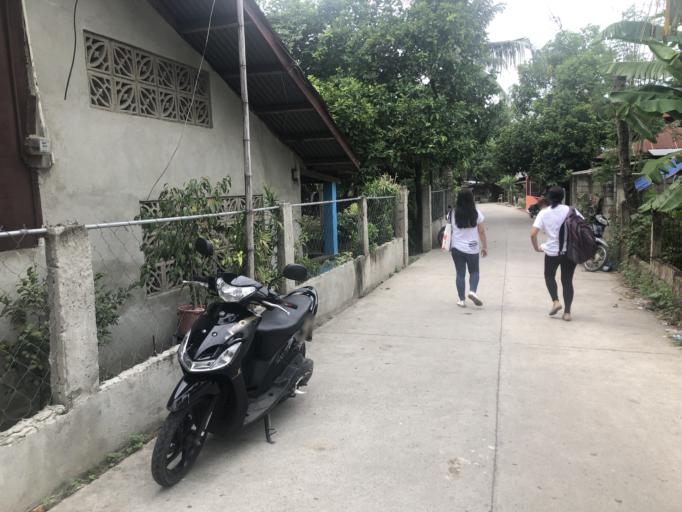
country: PH
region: Central Visayas
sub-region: Province of Negros Oriental
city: Dumaguete
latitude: 9.3037
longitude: 123.2989
